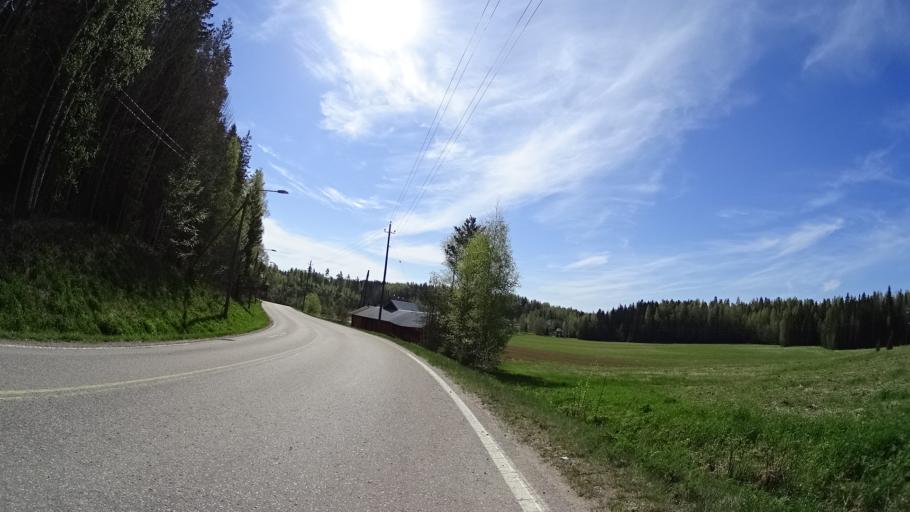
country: FI
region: Uusimaa
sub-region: Helsinki
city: Nurmijaervi
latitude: 60.3819
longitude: 24.8363
